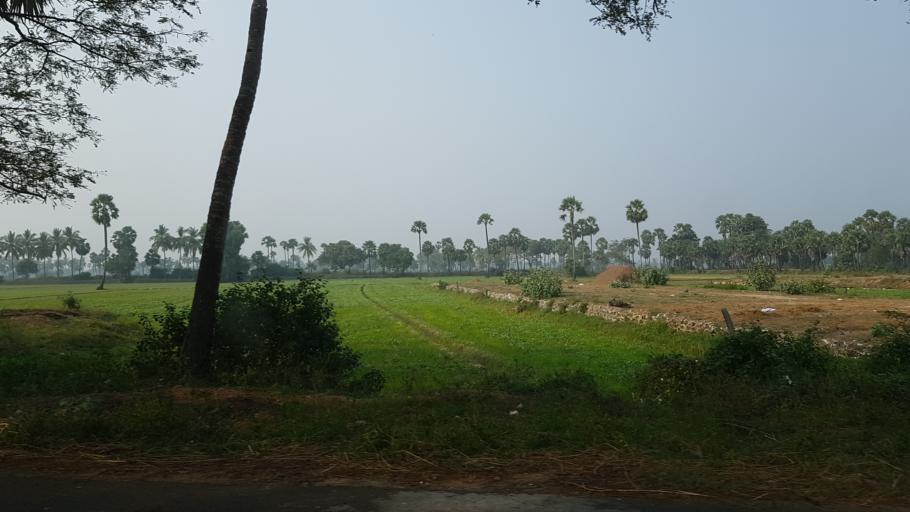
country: IN
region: Andhra Pradesh
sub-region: Krishna
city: Korukollu
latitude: 16.4910
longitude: 81.2545
